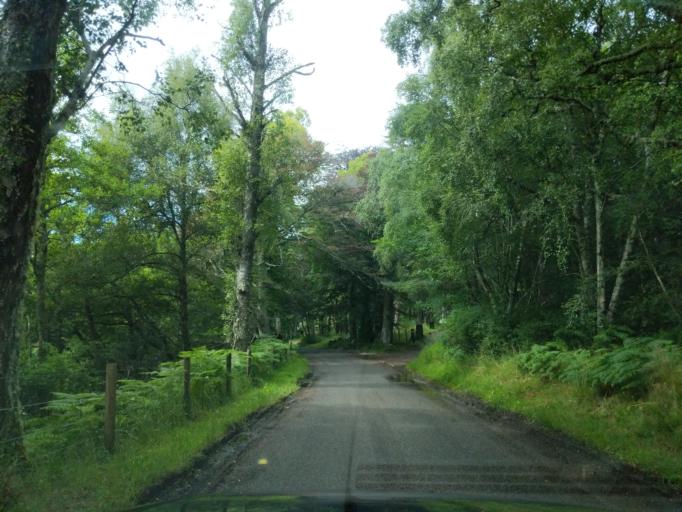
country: GB
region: Scotland
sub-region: Aberdeenshire
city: Aboyne
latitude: 57.0572
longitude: -2.8578
